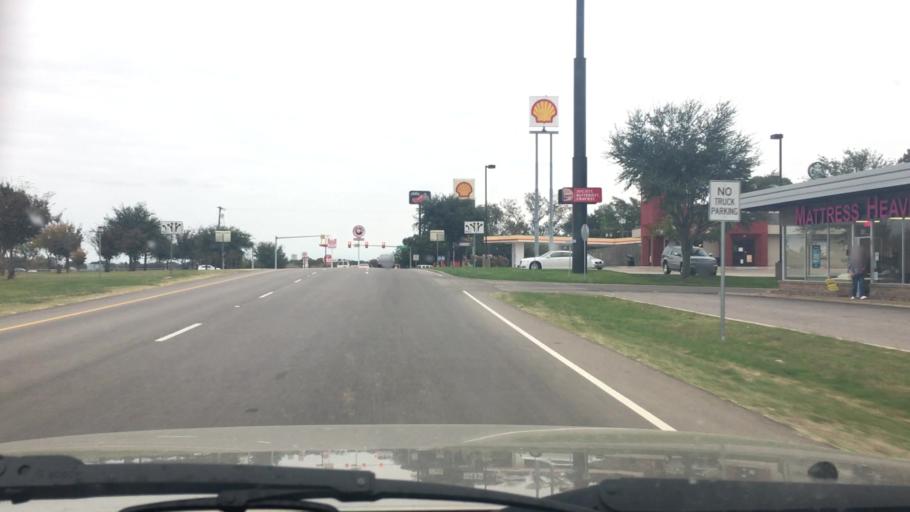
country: US
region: Texas
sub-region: Hopkins County
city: Sulphur Springs
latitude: 33.1158
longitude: -95.5984
